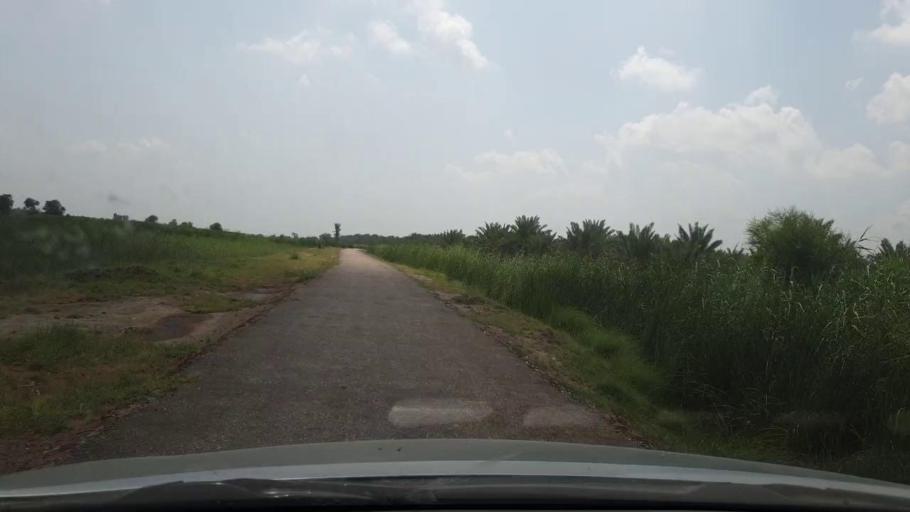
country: PK
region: Sindh
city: Kot Diji
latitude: 27.3954
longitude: 68.7239
